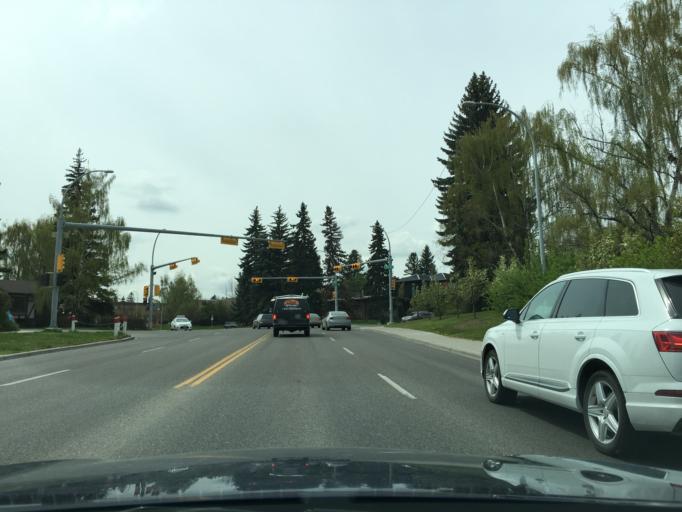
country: CA
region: Alberta
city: Calgary
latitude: 51.0118
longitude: -114.0808
